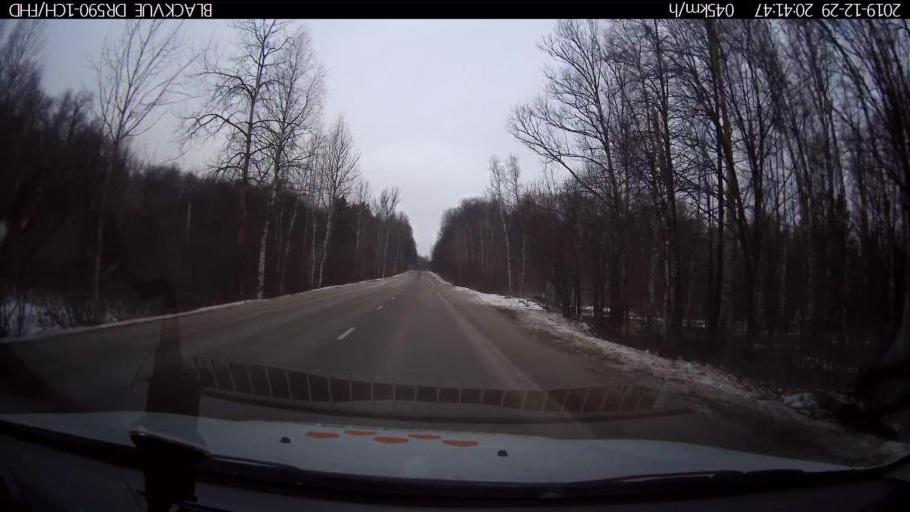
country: RU
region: Nizjnij Novgorod
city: Afonino
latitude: 56.1878
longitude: 44.0355
